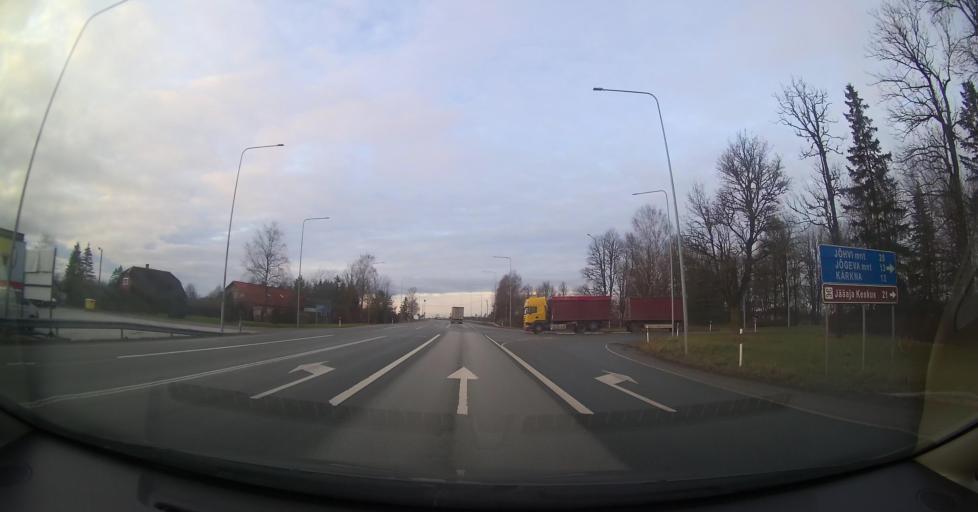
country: EE
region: Tartu
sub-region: Noo vald
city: Noo
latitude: 58.4298
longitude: 26.4864
